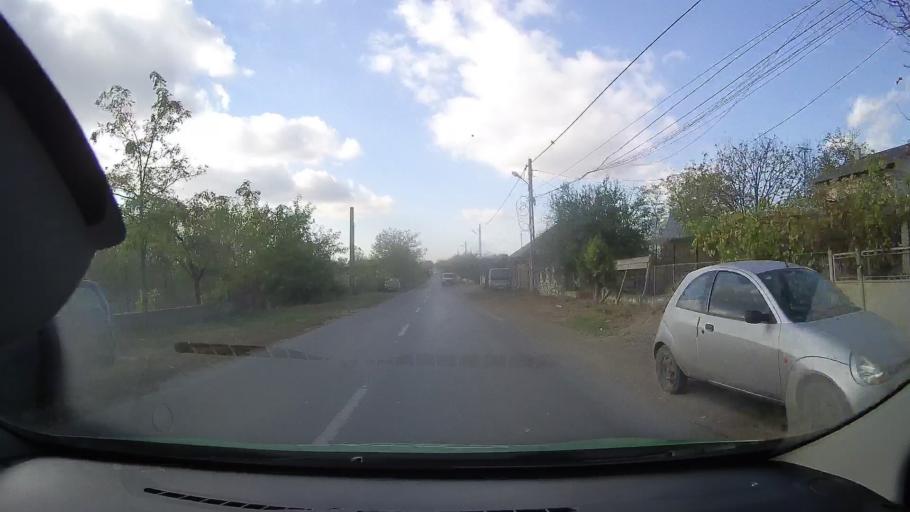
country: RO
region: Constanta
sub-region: Comuna Sacele
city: Sacele
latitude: 44.4899
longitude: 28.6492
